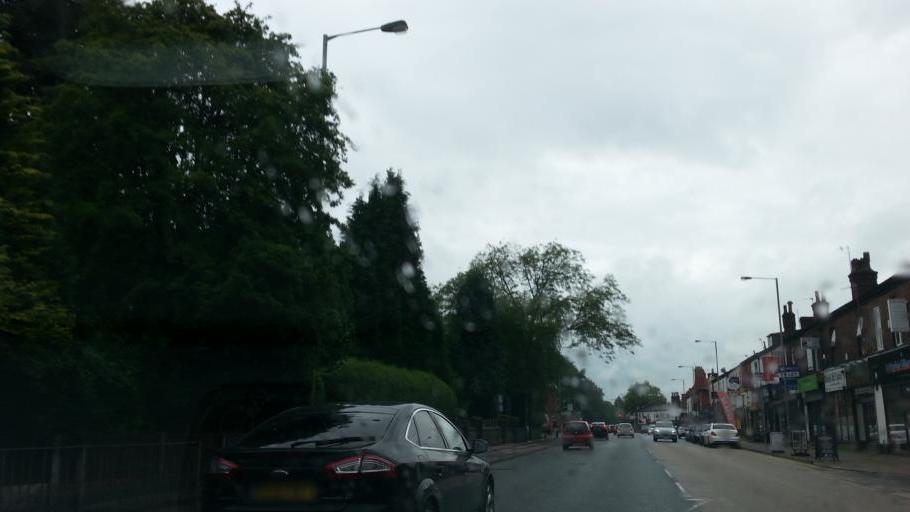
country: GB
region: England
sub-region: Borough of Bury
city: Whitefield
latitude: 53.5464
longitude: -2.2923
